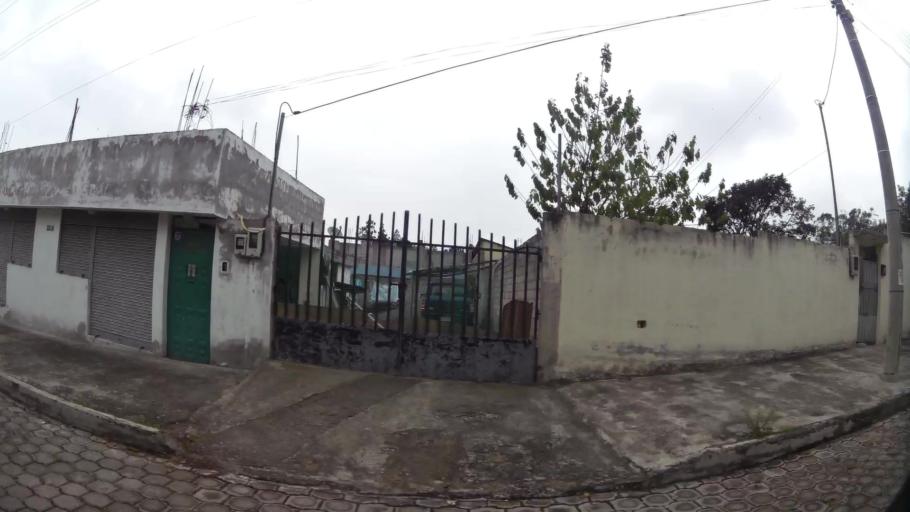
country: EC
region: Pichincha
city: Quito
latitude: -0.2710
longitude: -78.4782
